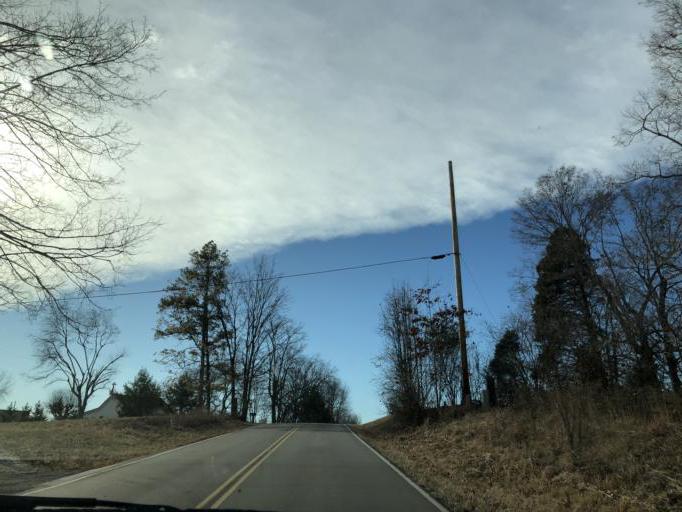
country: US
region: Tennessee
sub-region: Wilson County
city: Mount Juliet
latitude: 36.1630
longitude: -86.5518
